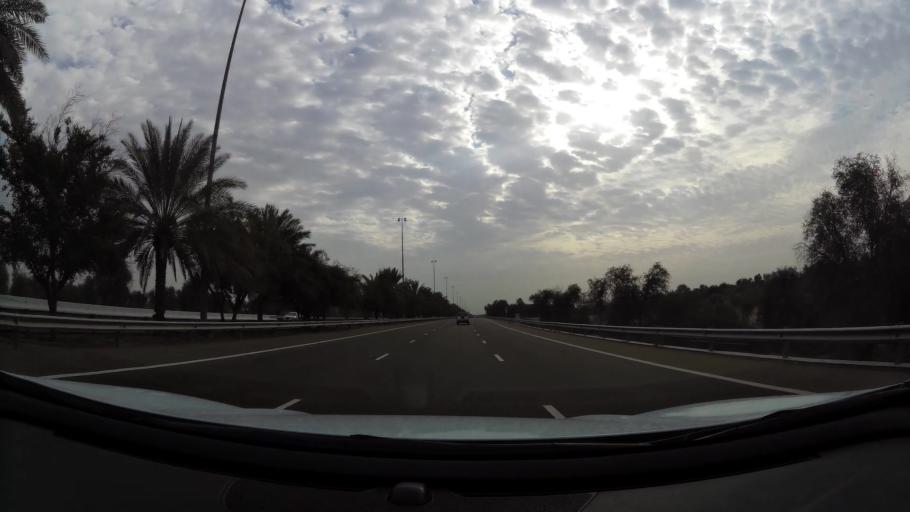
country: AE
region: Abu Dhabi
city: Al Ain
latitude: 24.1797
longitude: 55.1640
